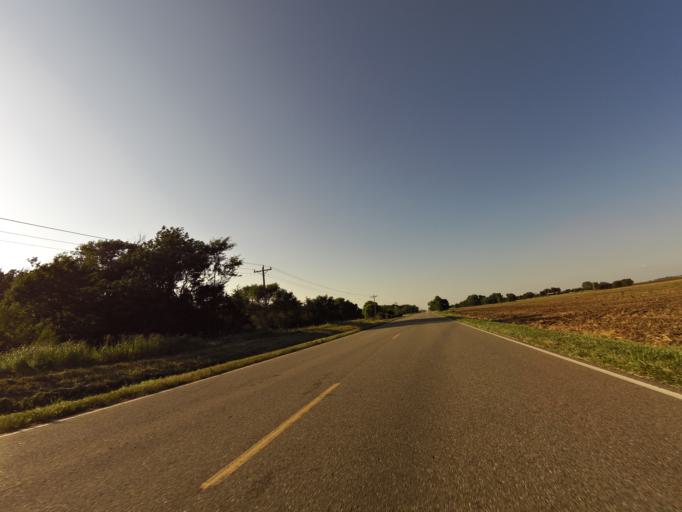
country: US
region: Kansas
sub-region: Reno County
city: Buhler
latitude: 38.1654
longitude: -97.8487
